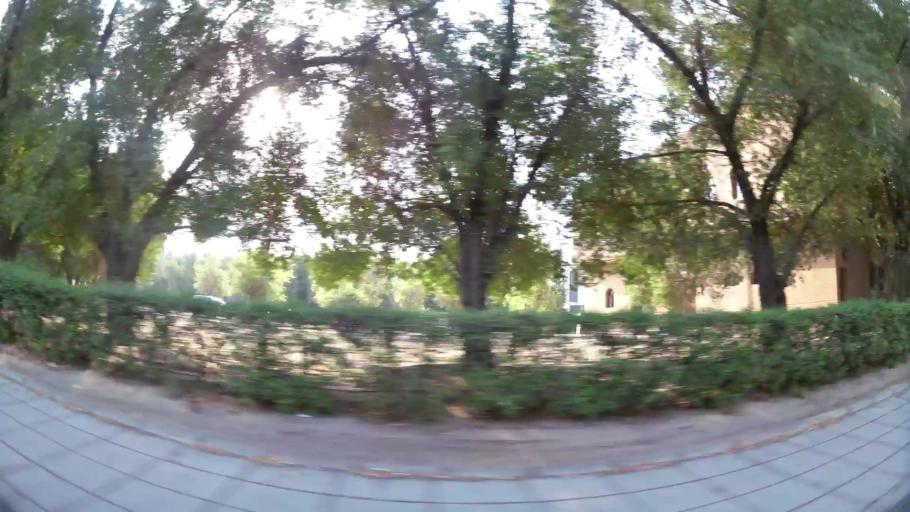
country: KW
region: Muhafazat Hawalli
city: Salwa
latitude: 29.2888
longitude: 48.0627
